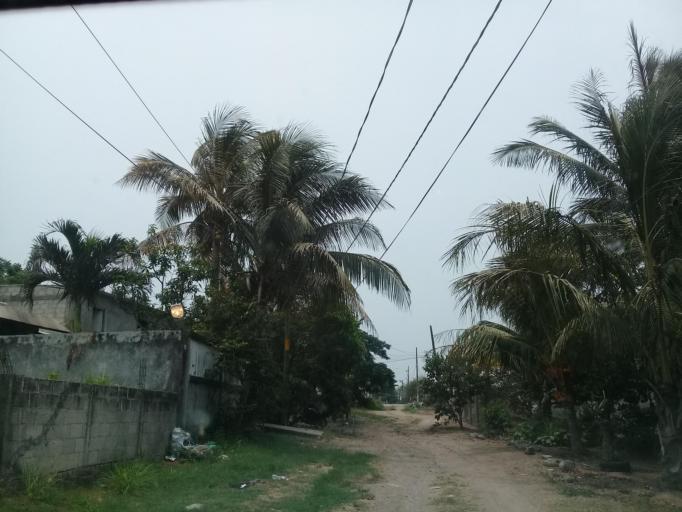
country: MX
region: Veracruz
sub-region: Veracruz
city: Las Amapolas
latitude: 19.1499
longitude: -96.2023
